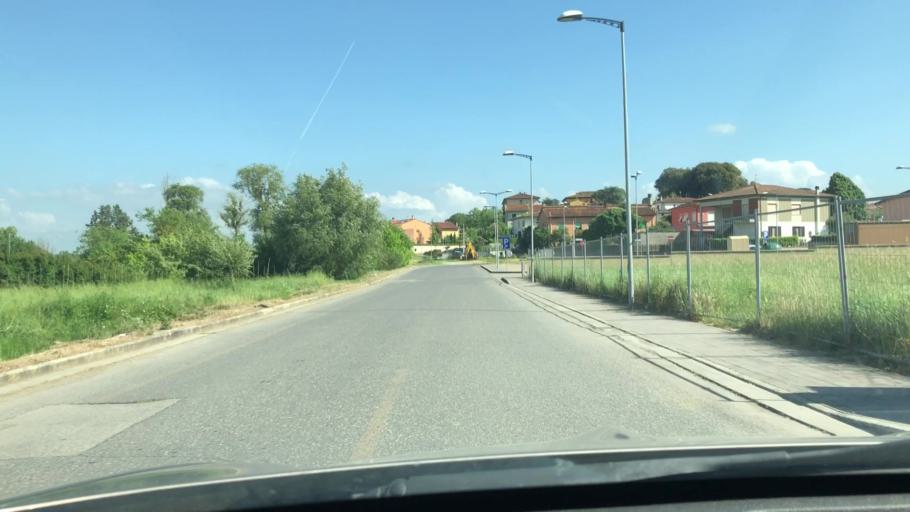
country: IT
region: Tuscany
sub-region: Province of Pisa
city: Capannoli
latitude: 43.5891
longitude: 10.6752
